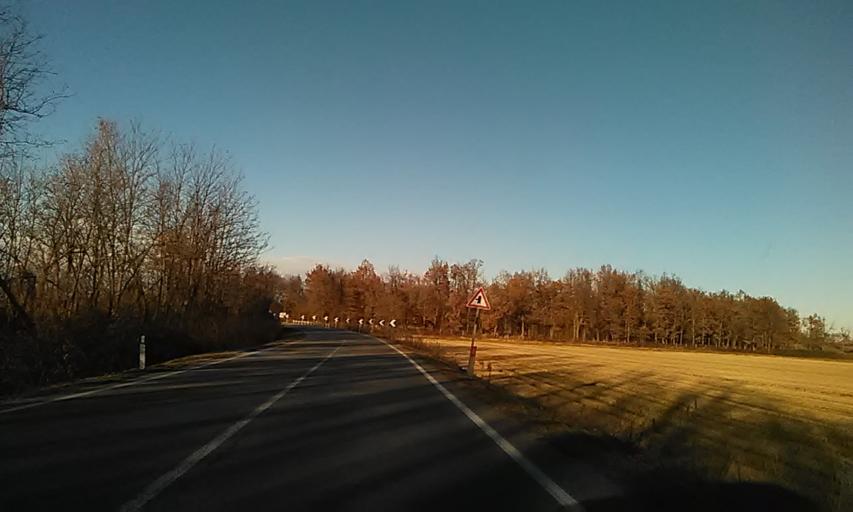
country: IT
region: Piedmont
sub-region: Provincia di Biella
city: Gifflenga
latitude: 45.4744
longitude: 8.2187
